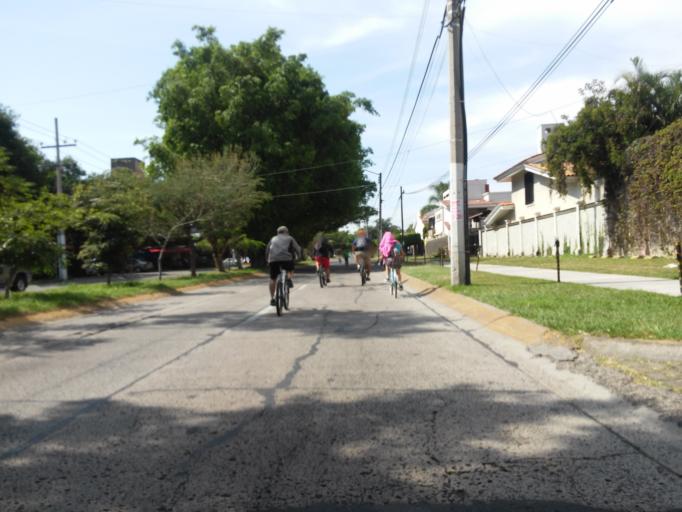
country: MX
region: Jalisco
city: Guadalajara
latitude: 20.6576
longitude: -103.4178
